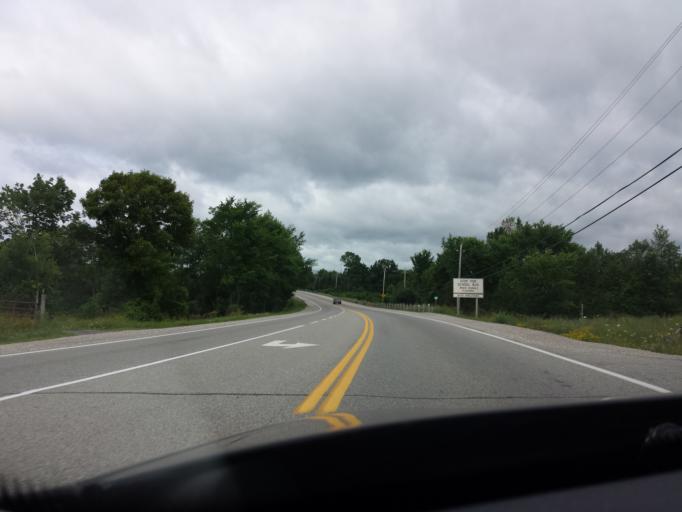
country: CA
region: Ontario
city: Carleton Place
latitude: 45.1327
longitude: -76.1765
